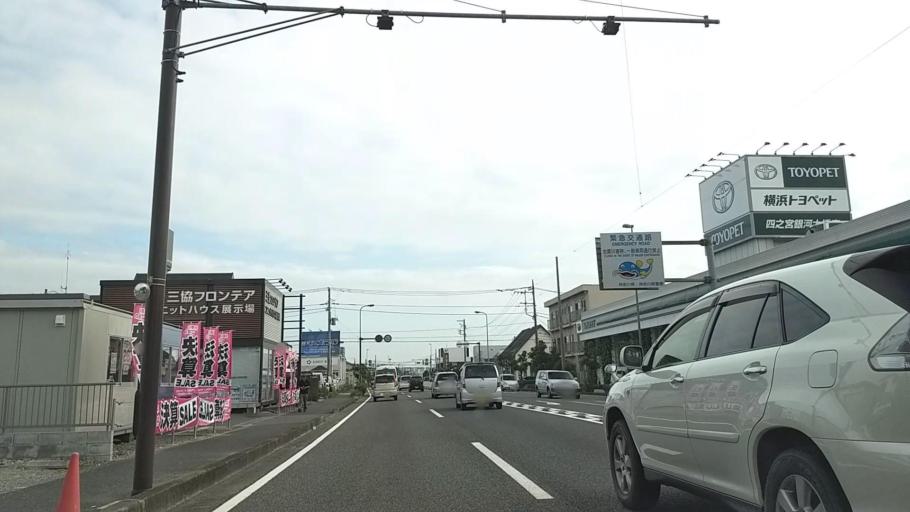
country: JP
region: Kanagawa
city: Hiratsuka
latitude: 35.3513
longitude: 139.3565
